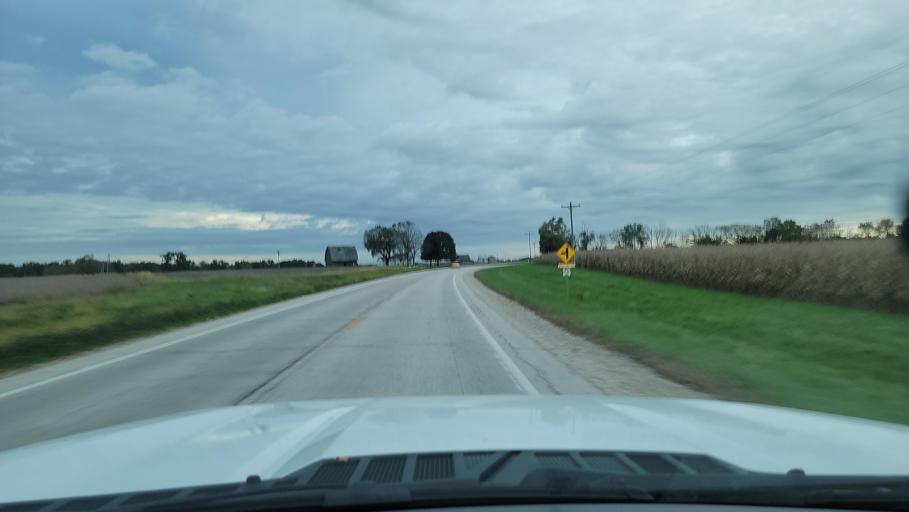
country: US
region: Illinois
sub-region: Schuyler County
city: Rushville
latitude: 40.0925
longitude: -90.6059
